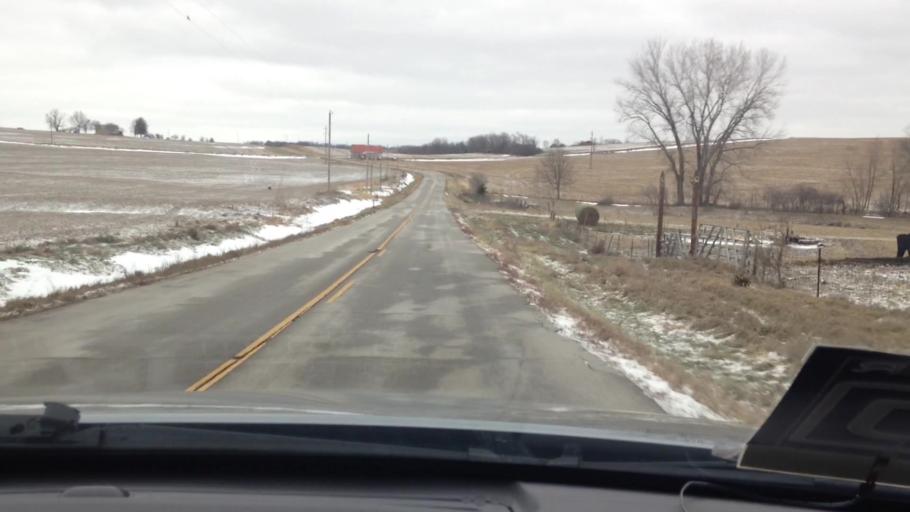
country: US
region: Missouri
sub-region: Platte County
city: Weston
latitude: 39.4567
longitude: -94.8464
